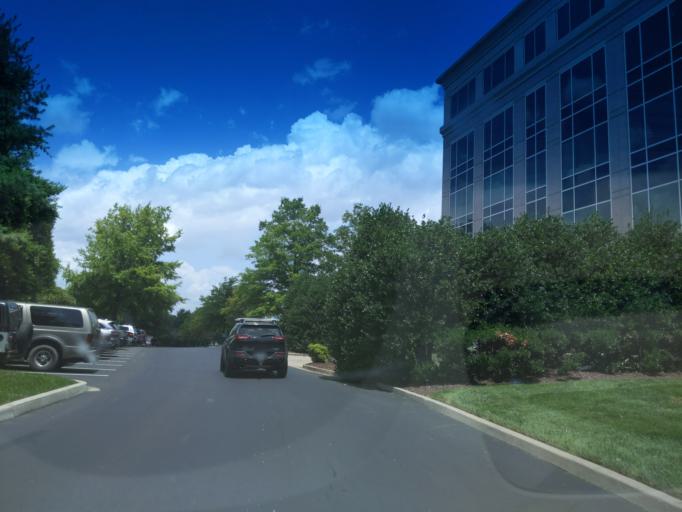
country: US
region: Tennessee
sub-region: Williamson County
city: Brentwood
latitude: 36.0423
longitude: -86.7707
